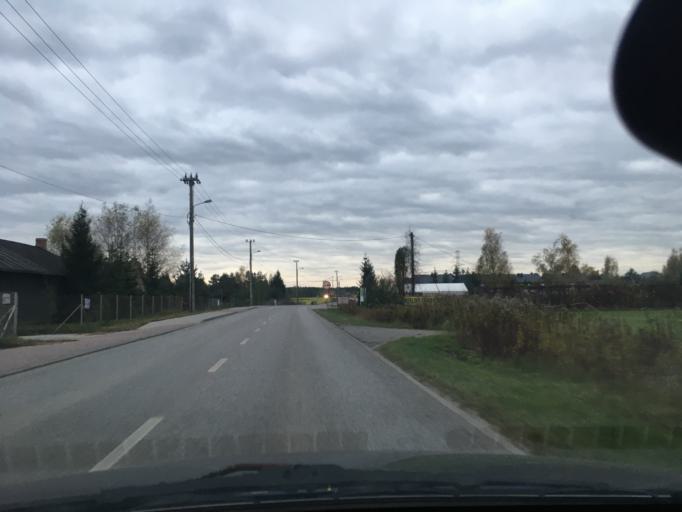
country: PL
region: Masovian Voivodeship
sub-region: Powiat piaseczynski
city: Lesznowola
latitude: 52.0758
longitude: 20.9364
